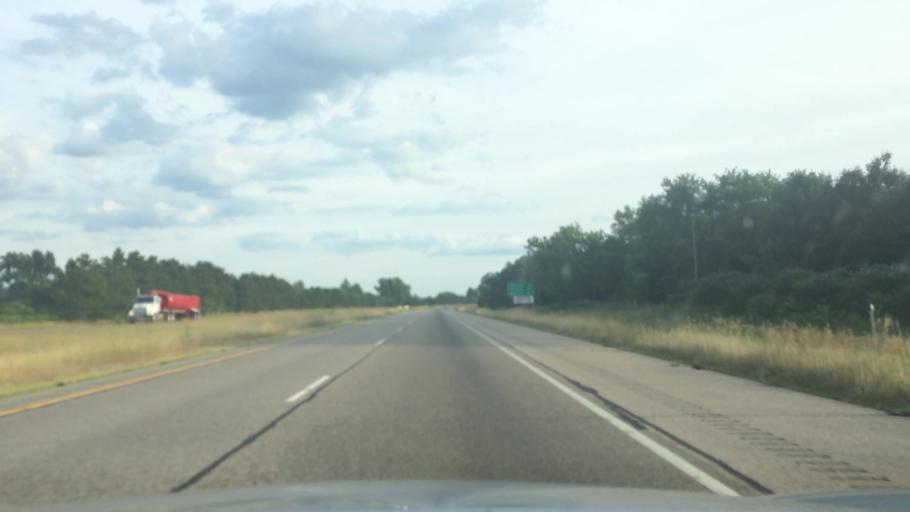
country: US
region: Wisconsin
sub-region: Portage County
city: Plover
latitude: 44.2024
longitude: -89.5234
